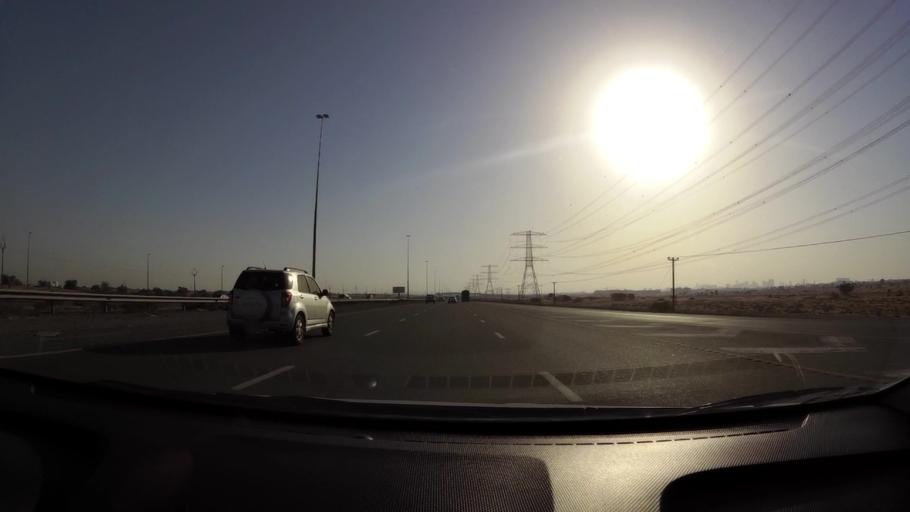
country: AE
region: Ajman
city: Ajman
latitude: 25.3621
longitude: 55.5294
